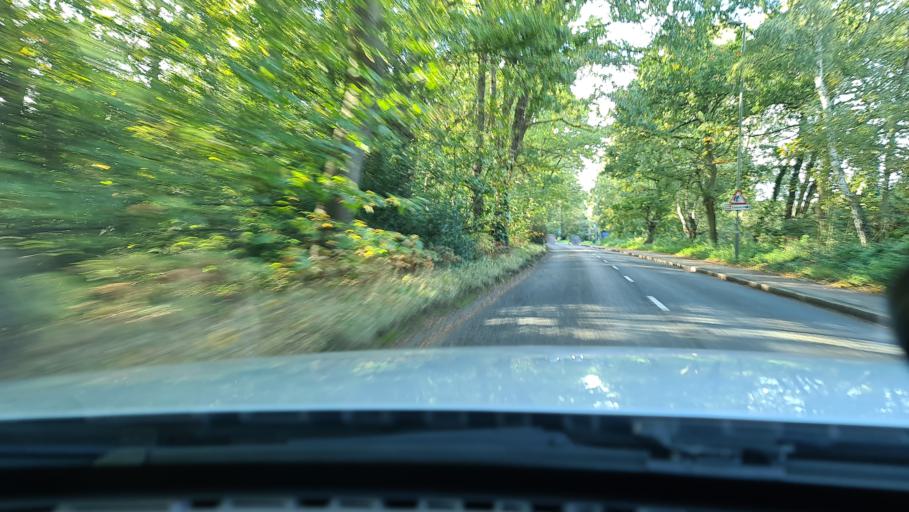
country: GB
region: England
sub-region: Surrey
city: Walton-on-Thames
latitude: 51.3701
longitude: -0.4164
